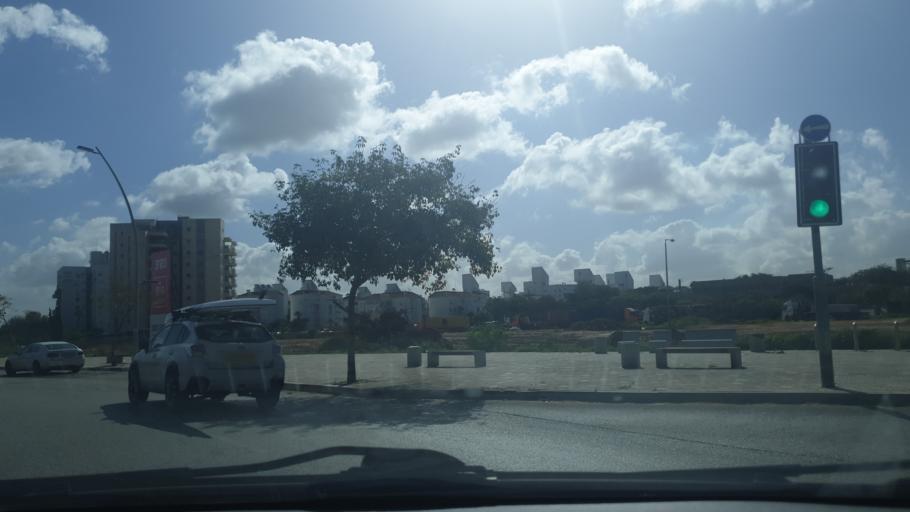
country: IL
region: Haifa
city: Qesarya
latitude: 32.5034
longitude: 34.9188
